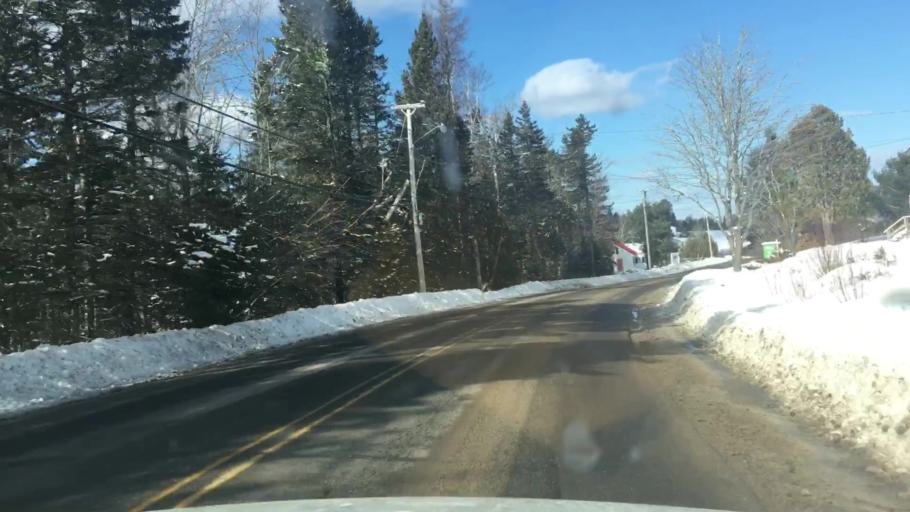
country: US
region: Maine
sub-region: Washington County
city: Machias
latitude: 44.6934
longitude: -67.4674
